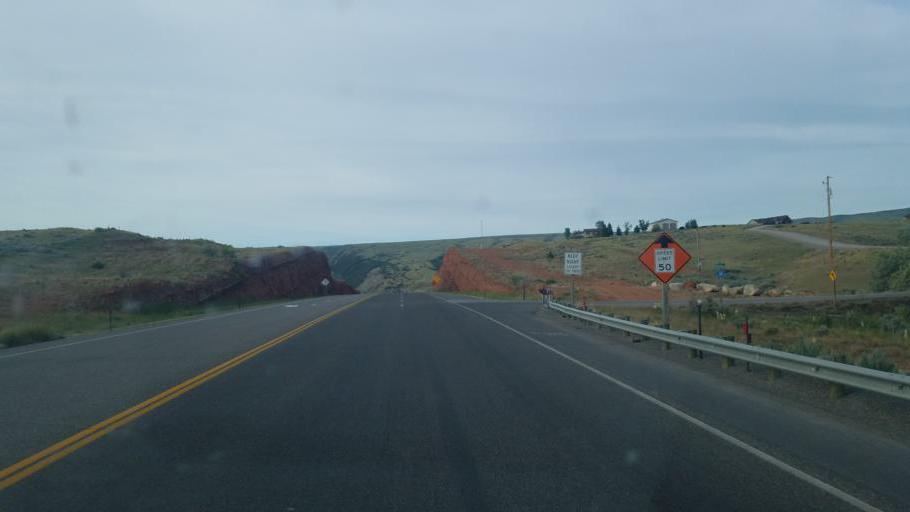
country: US
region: Wyoming
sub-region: Hot Springs County
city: Thermopolis
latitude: 43.6035
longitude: -108.2158
